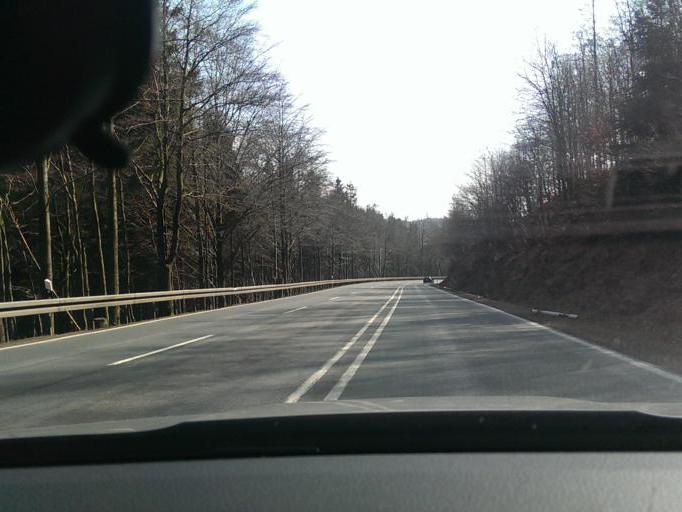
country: DE
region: Thuringia
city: Zella-Mehlis
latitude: 50.6747
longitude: 10.6854
